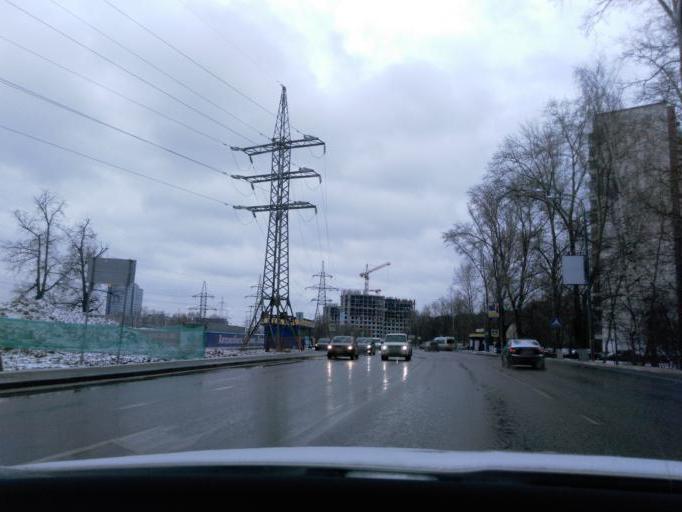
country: RU
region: Moscow
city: Khimki
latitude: 55.9001
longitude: 37.4173
